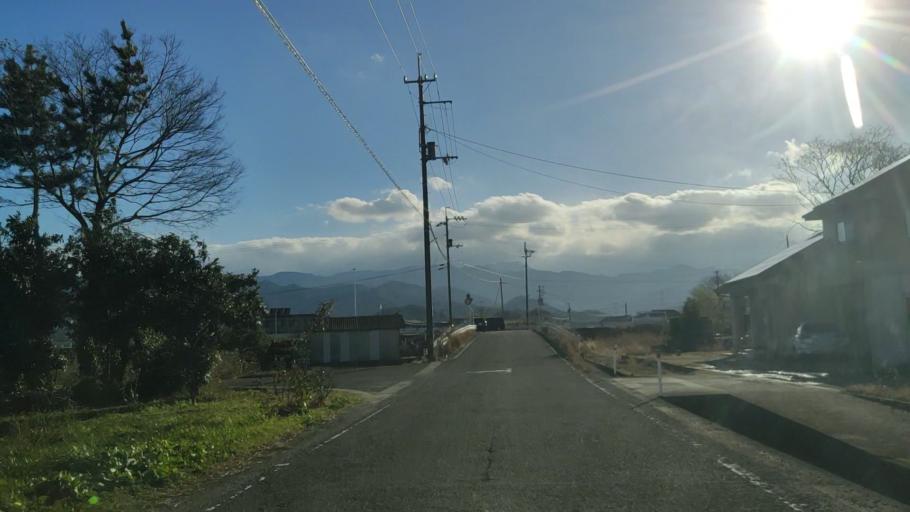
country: JP
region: Ehime
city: Saijo
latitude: 33.9091
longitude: 133.0970
